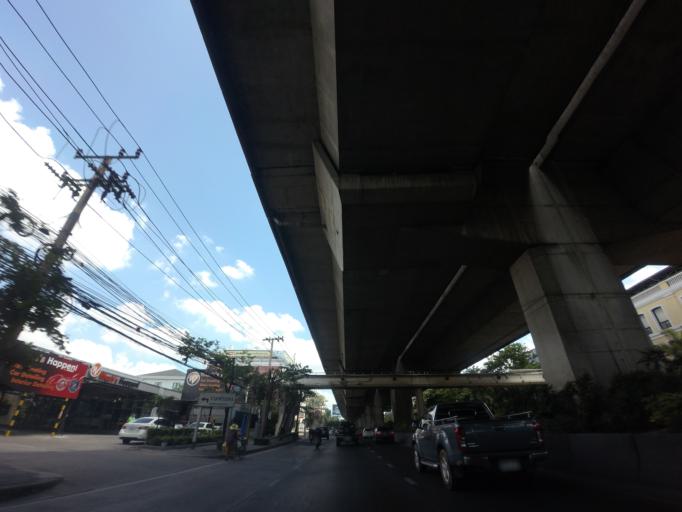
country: TH
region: Bangkok
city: Suan Luang
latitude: 13.7421
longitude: 100.6312
